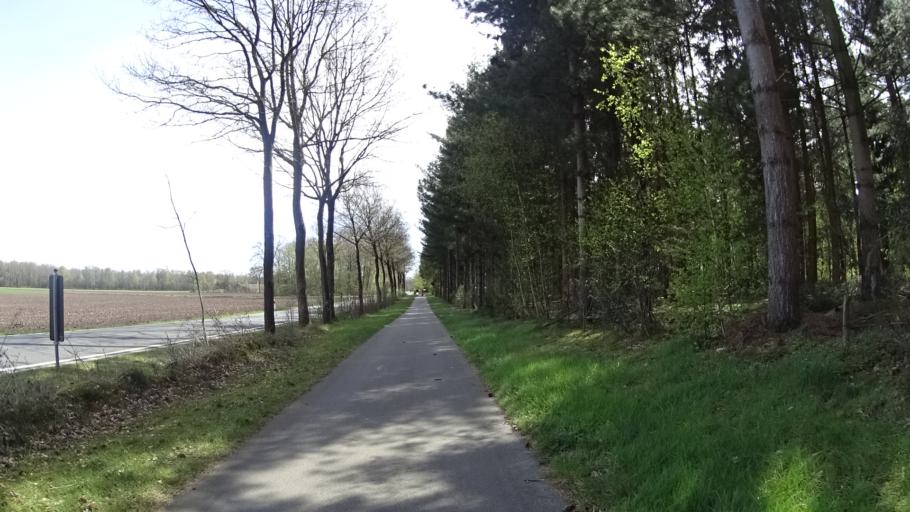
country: DE
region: Lower Saxony
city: Spelle
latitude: 52.3376
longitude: 7.4521
